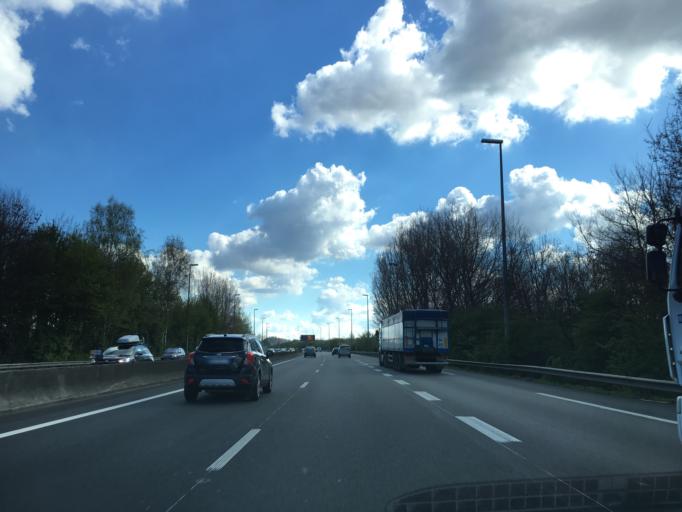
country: FR
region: Nord-Pas-de-Calais
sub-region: Departement du Pas-de-Calais
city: Dourges
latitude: 50.4509
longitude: 2.9706
